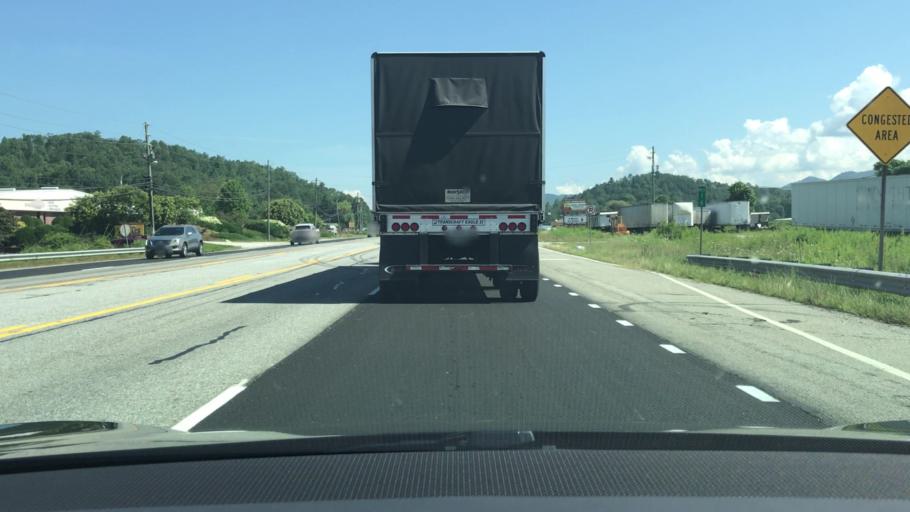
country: US
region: Georgia
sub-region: Rabun County
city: Mountain City
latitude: 34.9386
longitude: -83.3883
